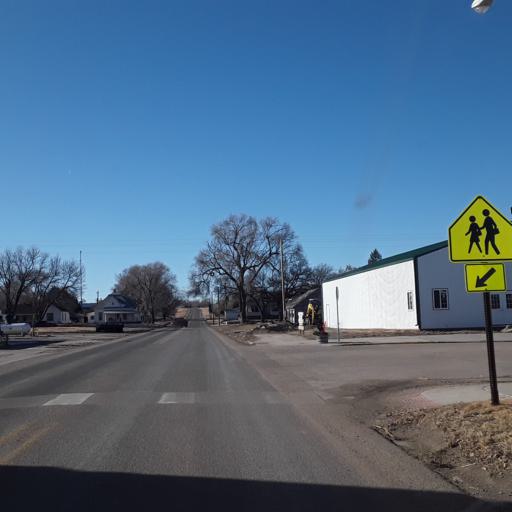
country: US
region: Nebraska
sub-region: Frontier County
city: Stockville
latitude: 40.6576
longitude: -100.6217
